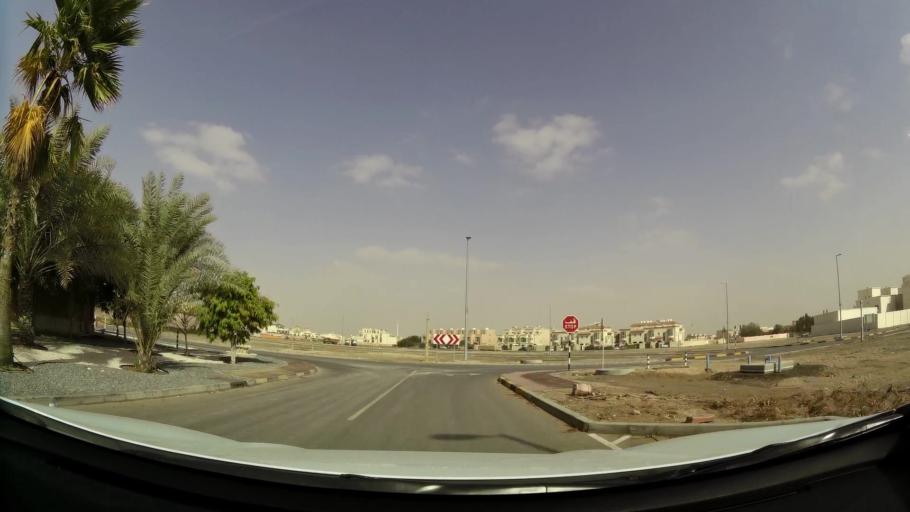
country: AE
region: Abu Dhabi
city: Abu Dhabi
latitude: 24.4278
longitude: 54.5972
